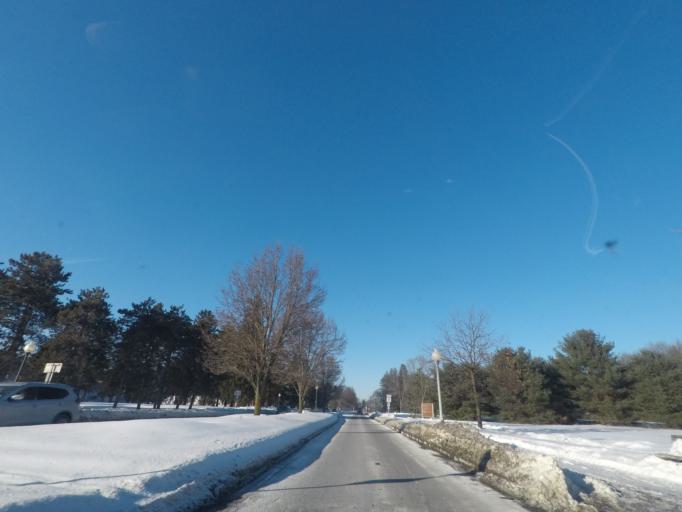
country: US
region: New York
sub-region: Saratoga County
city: Saratoga Springs
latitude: 43.0633
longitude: -73.7883
